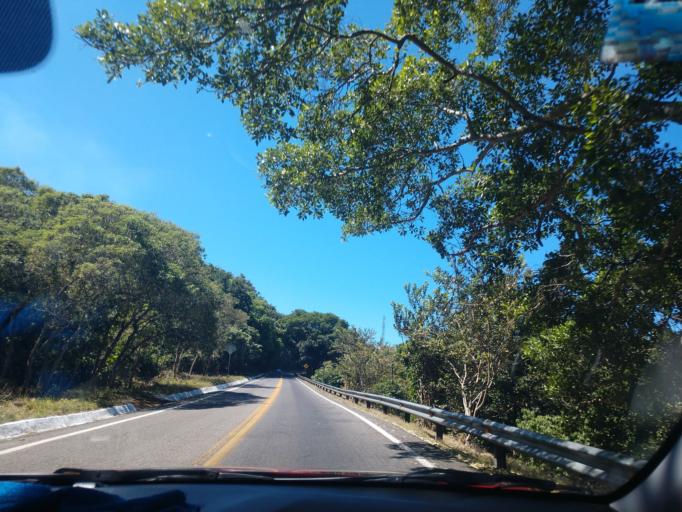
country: MX
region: Nayarit
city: Xalisco
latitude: 21.3710
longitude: -104.9000
